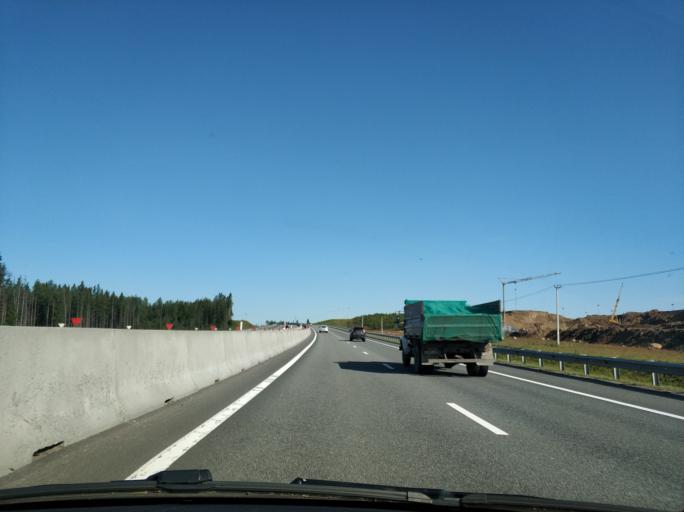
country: RU
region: Leningrad
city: Sosnovo
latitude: 60.5098
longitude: 30.1898
